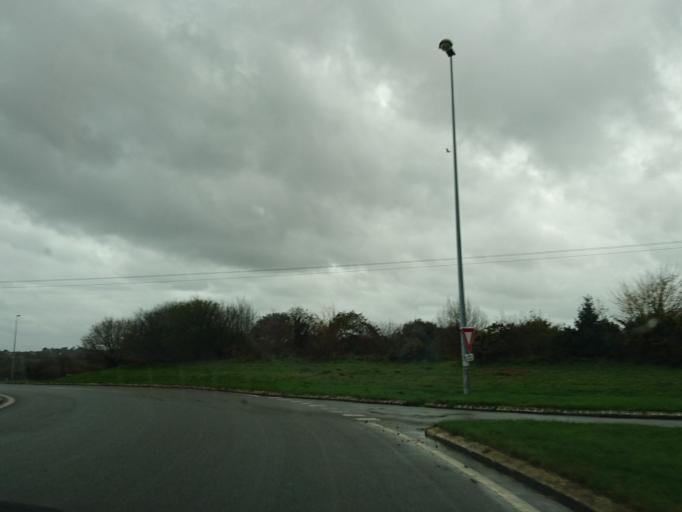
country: FR
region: Brittany
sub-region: Departement du Finistere
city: Guilers
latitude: 48.3736
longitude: -4.5615
